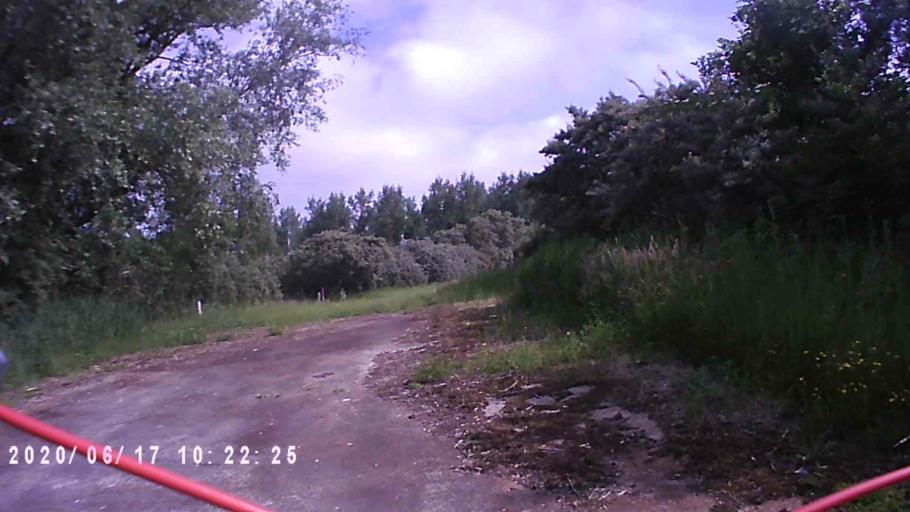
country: NL
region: Groningen
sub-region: Gemeente De Marne
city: Ulrum
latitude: 53.3905
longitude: 6.2512
